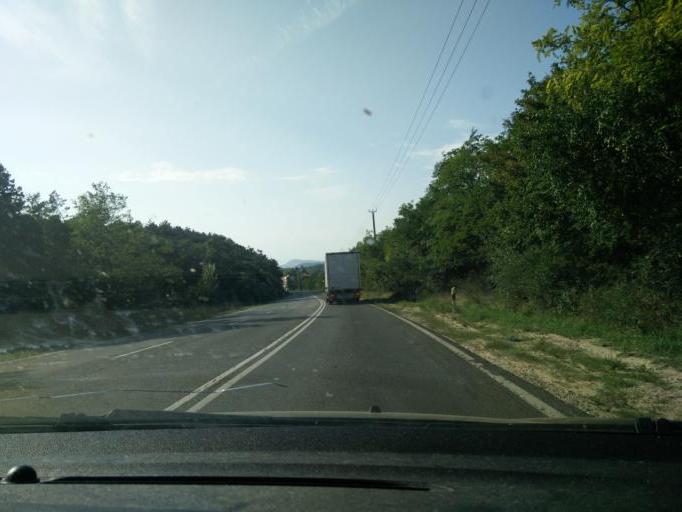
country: HU
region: Pest
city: Piliscsaba
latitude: 47.6263
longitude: 18.8592
